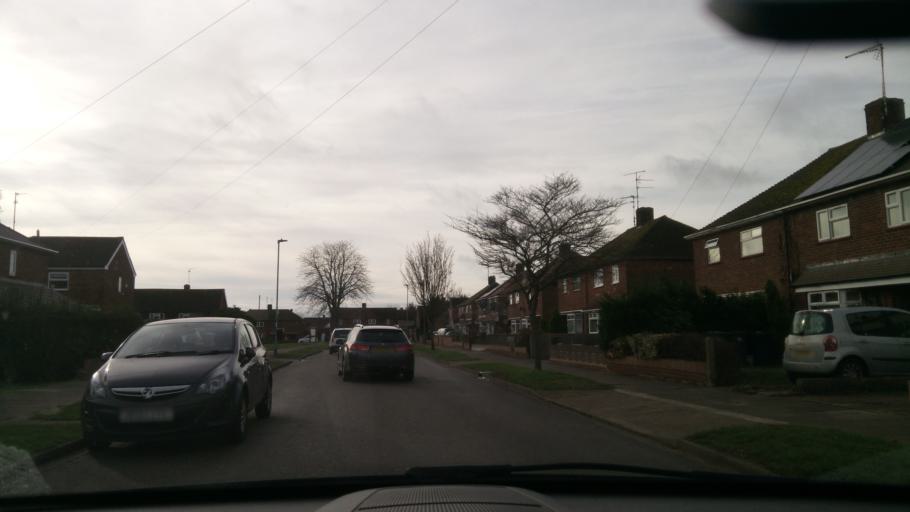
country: GB
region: England
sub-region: Peterborough
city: Peterborough
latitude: 52.5836
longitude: -0.2247
